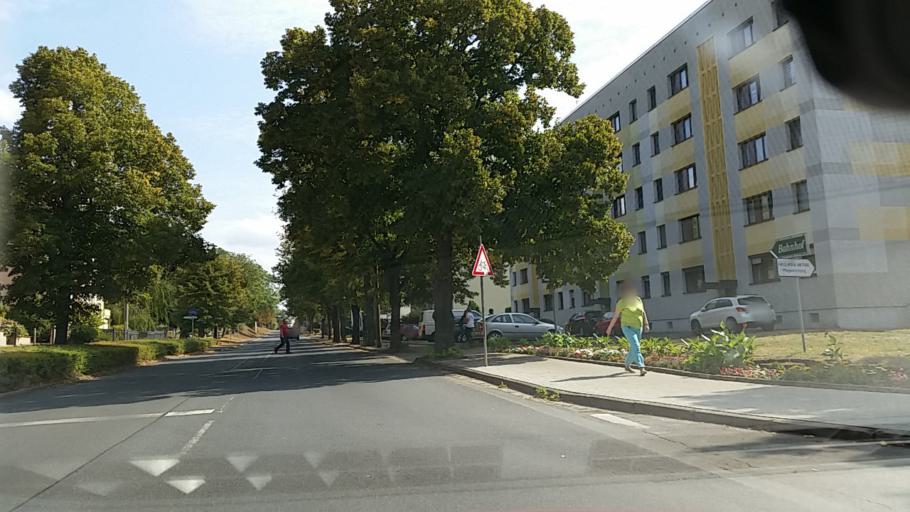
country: DE
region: Thuringia
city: Artern
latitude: 51.3644
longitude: 11.2973
